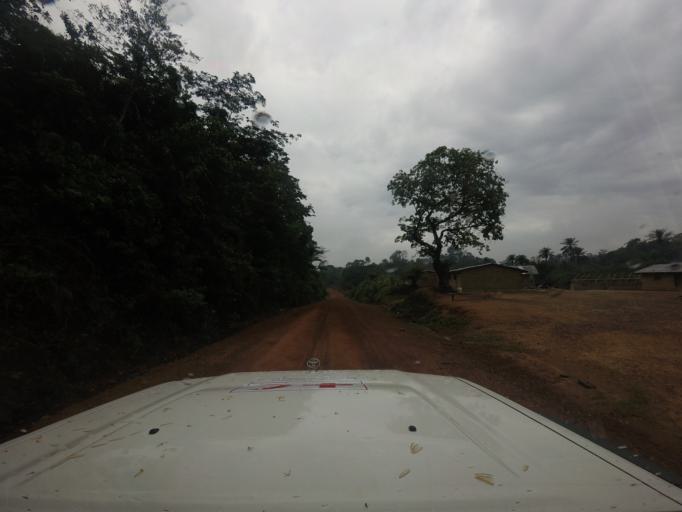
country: LR
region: Lofa
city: Voinjama
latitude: 8.3832
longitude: -9.8338
